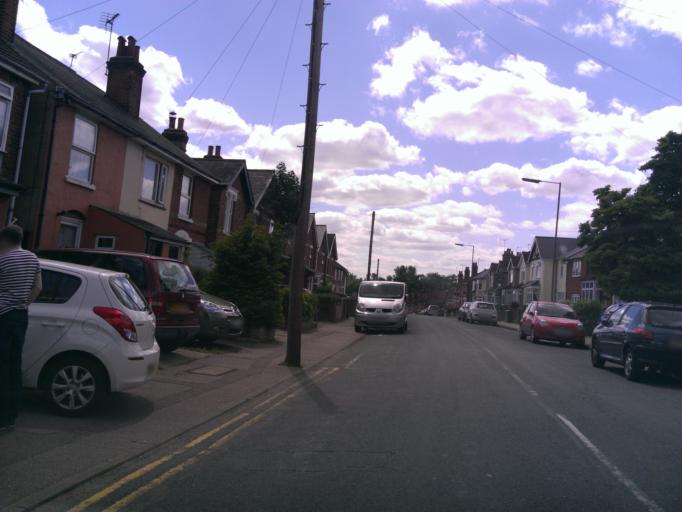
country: GB
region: England
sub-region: Essex
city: Colchester
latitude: 51.8795
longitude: 0.9134
